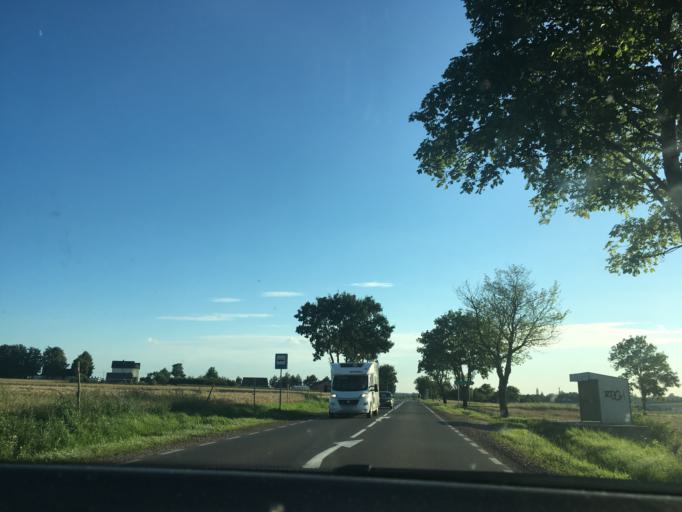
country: PL
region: Masovian Voivodeship
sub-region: Powiat losicki
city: Losice
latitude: 52.2253
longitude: 22.7449
